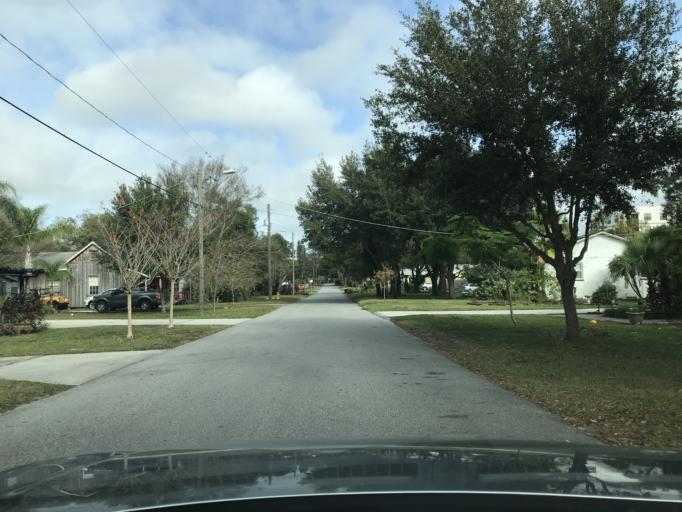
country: US
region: Florida
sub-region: Hillsborough County
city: Egypt Lake-Leto
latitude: 28.0004
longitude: -82.4609
